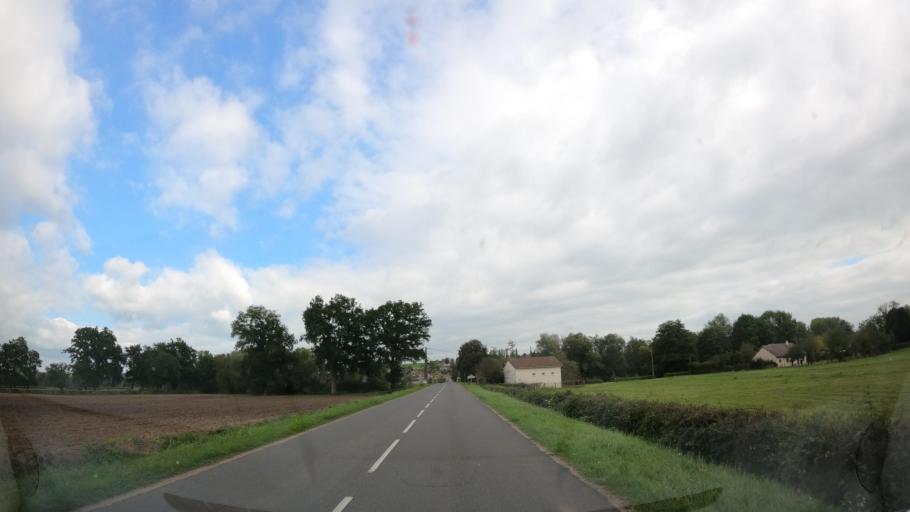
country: FR
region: Auvergne
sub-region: Departement de l'Allier
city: Lapalisse
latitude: 46.3271
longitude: 3.5874
